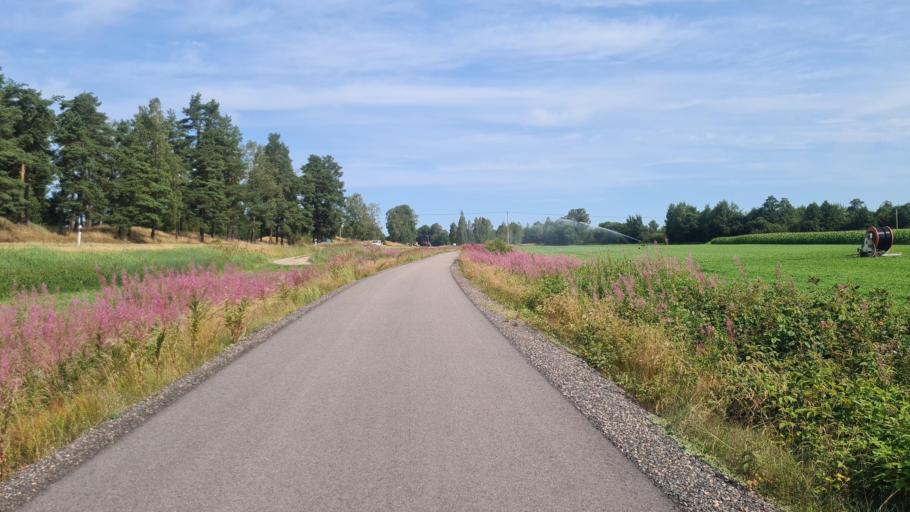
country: SE
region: Kronoberg
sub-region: Ljungby Kommun
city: Lagan
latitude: 56.8674
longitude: 13.9774
